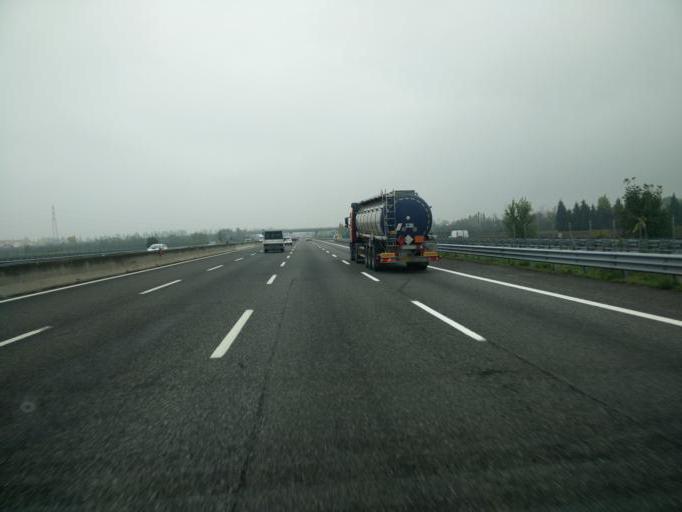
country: IT
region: Emilia-Romagna
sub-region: Provincia di Modena
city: Baggiovara
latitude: 44.6243
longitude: 10.8813
